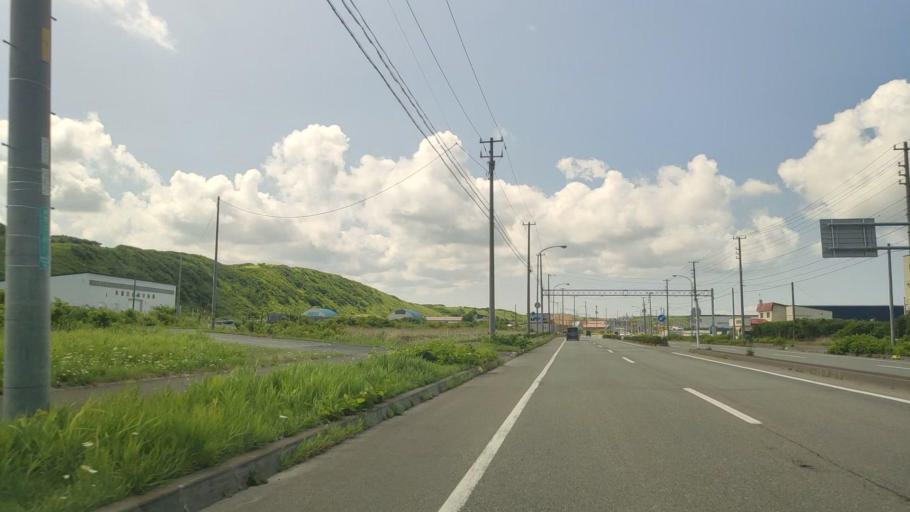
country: JP
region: Hokkaido
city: Wakkanai
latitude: 45.4023
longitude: 141.7446
